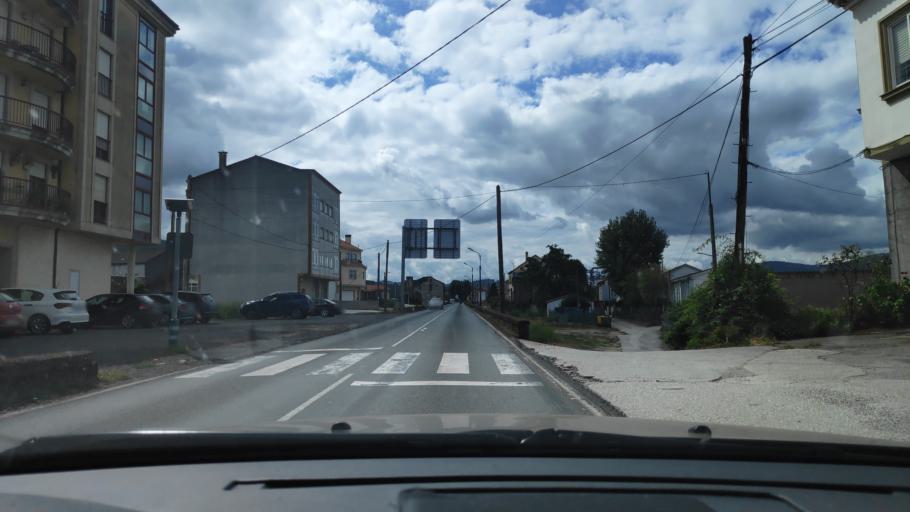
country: ES
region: Galicia
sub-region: Provincia da Coruna
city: Padron
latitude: 42.7286
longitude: -8.6571
